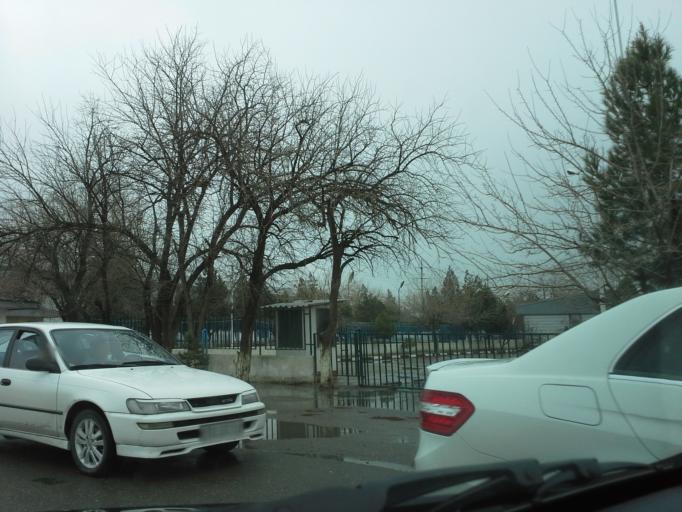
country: TM
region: Ahal
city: Ashgabat
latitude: 37.9477
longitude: 58.4341
